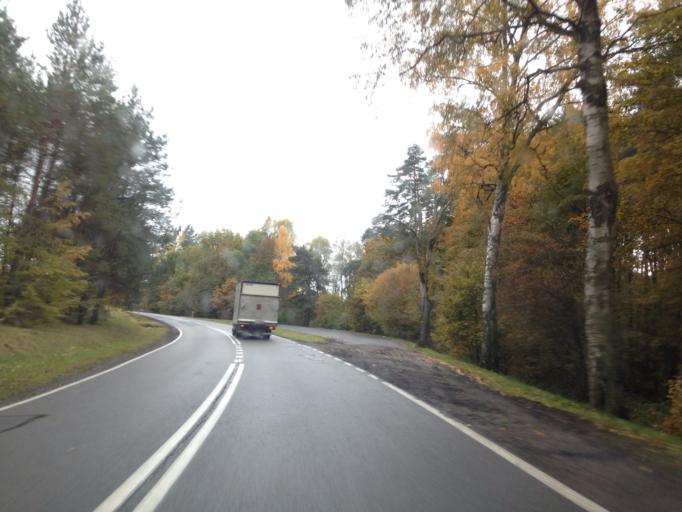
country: PL
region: Pomeranian Voivodeship
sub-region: Powiat kwidzynski
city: Ryjewo
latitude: 53.8563
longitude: 19.0002
